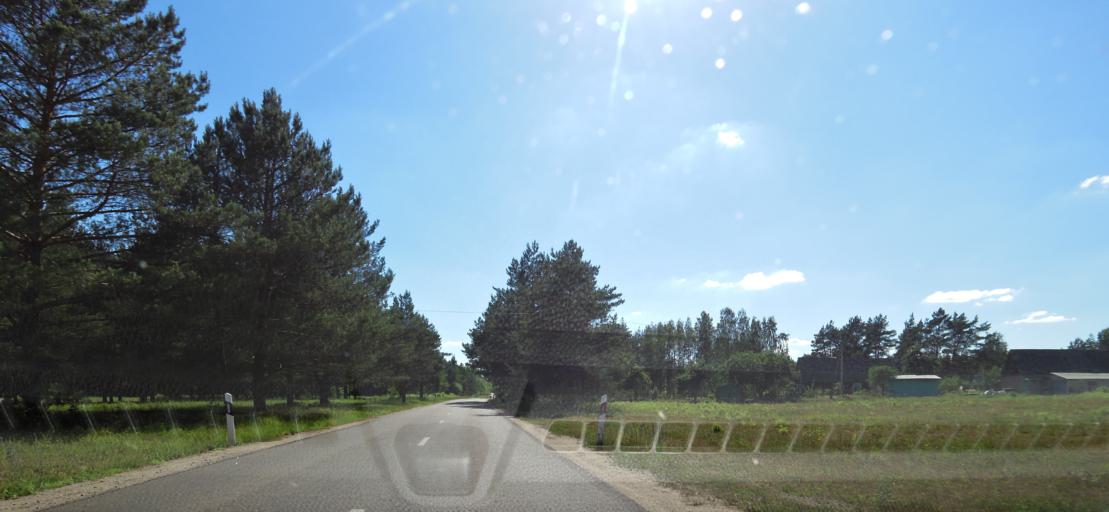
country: LT
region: Vilnius County
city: Rasos
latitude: 54.7577
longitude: 25.3417
